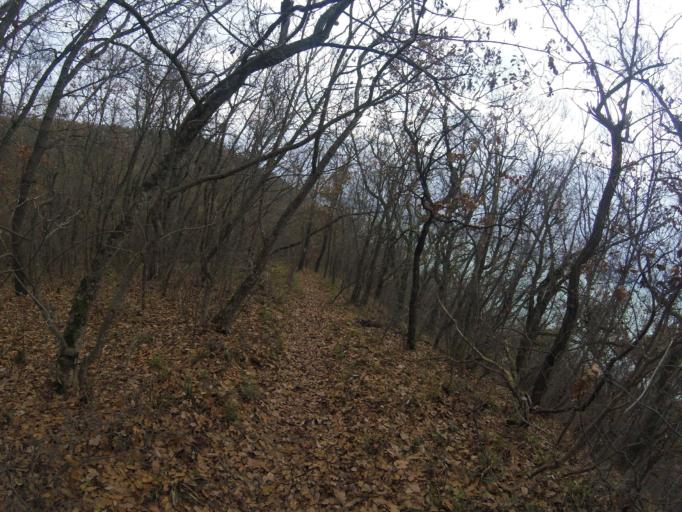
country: HU
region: Veszprem
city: Tihany
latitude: 46.8945
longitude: 17.8727
